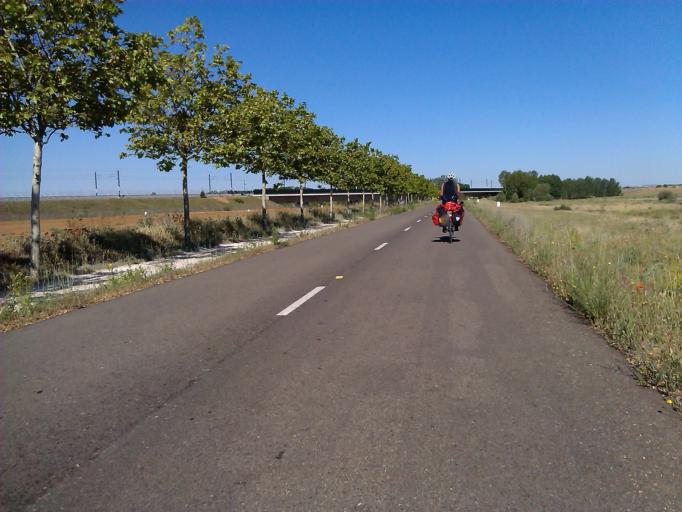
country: ES
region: Castille and Leon
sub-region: Provincia de Leon
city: Calzada del Coto
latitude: 42.3844
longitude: -5.1051
